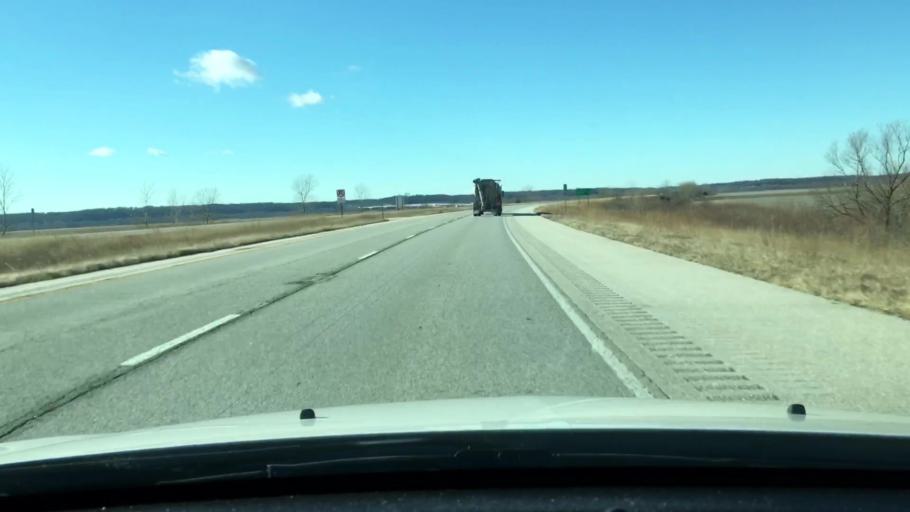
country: US
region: Illinois
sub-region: Pike County
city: Griggsville
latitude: 39.6855
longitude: -90.5863
